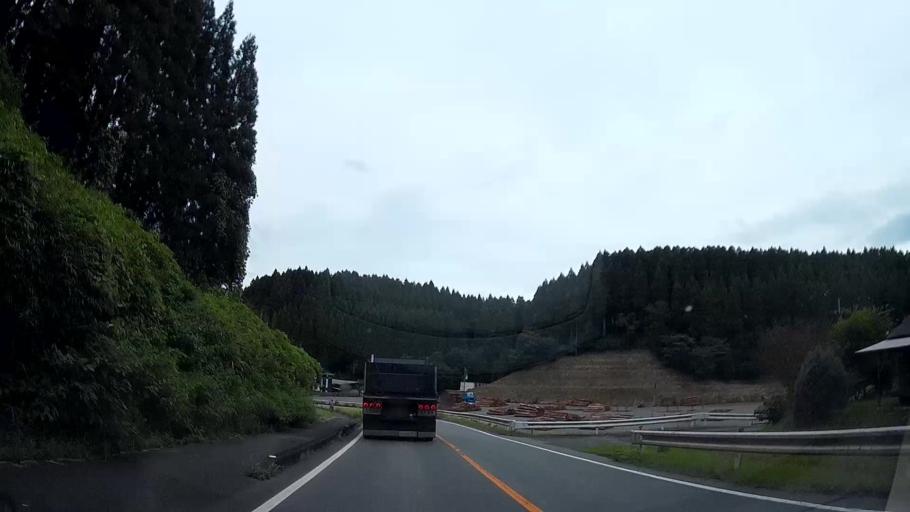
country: JP
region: Oita
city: Tsukawaki
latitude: 33.1253
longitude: 131.0564
